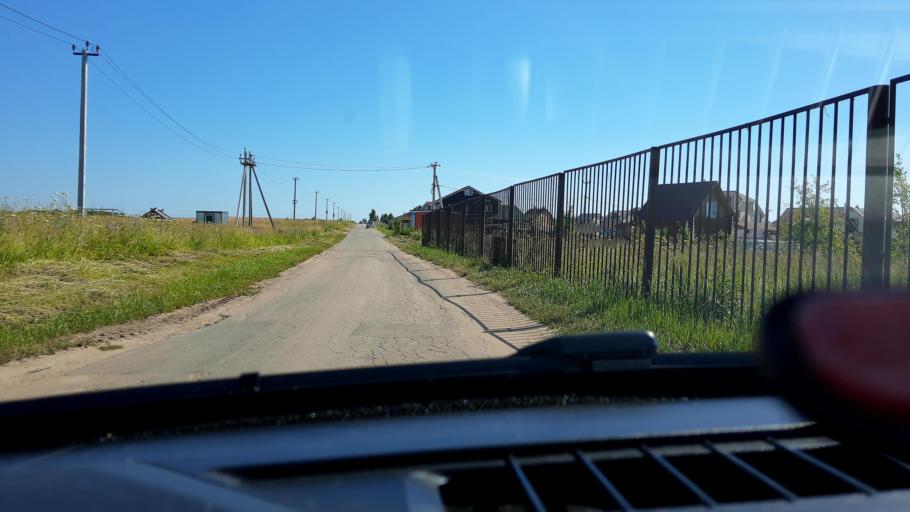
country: RU
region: Nizjnij Novgorod
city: Babino
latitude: 56.1246
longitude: 43.6253
